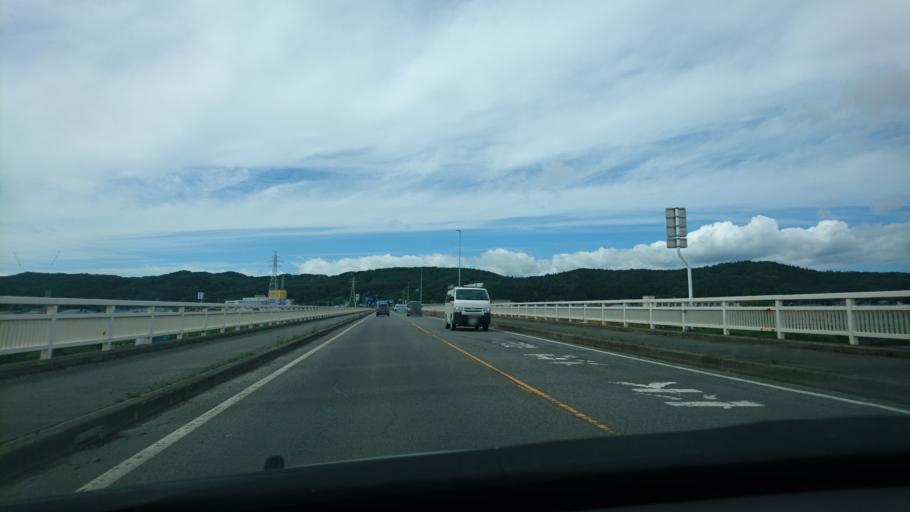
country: JP
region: Aomori
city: Hachinohe
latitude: 40.1930
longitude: 141.7852
